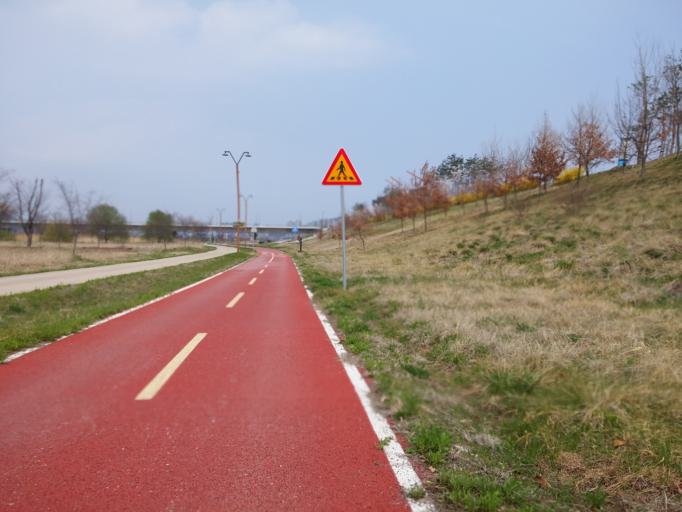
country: KR
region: Daejeon
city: Songgang-dong
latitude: 36.4732
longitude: 127.2688
